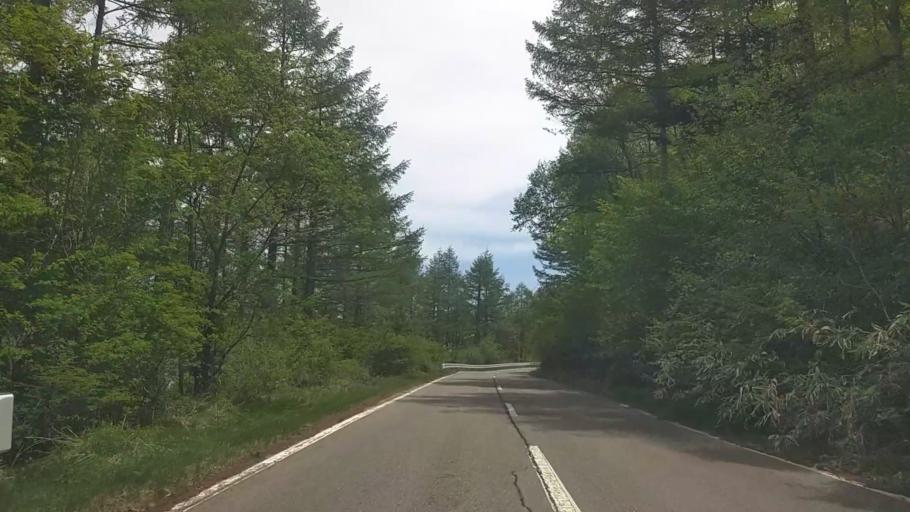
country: JP
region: Nagano
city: Saku
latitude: 36.0970
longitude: 138.3873
